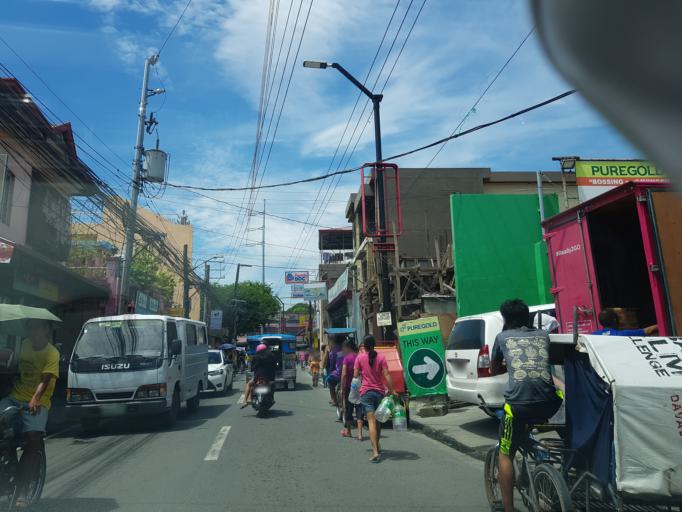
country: PH
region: Calabarzon
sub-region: Province of Rizal
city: Taguig
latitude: 14.5092
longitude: 121.0668
